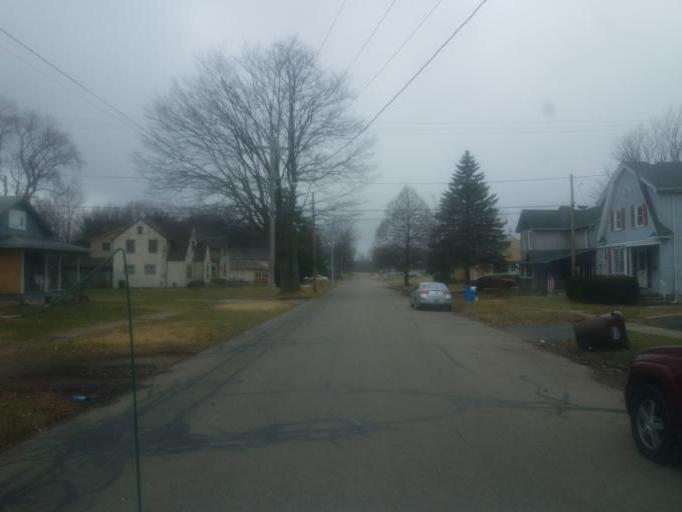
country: US
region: Ohio
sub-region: Crawford County
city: Galion
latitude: 40.7301
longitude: -82.7992
